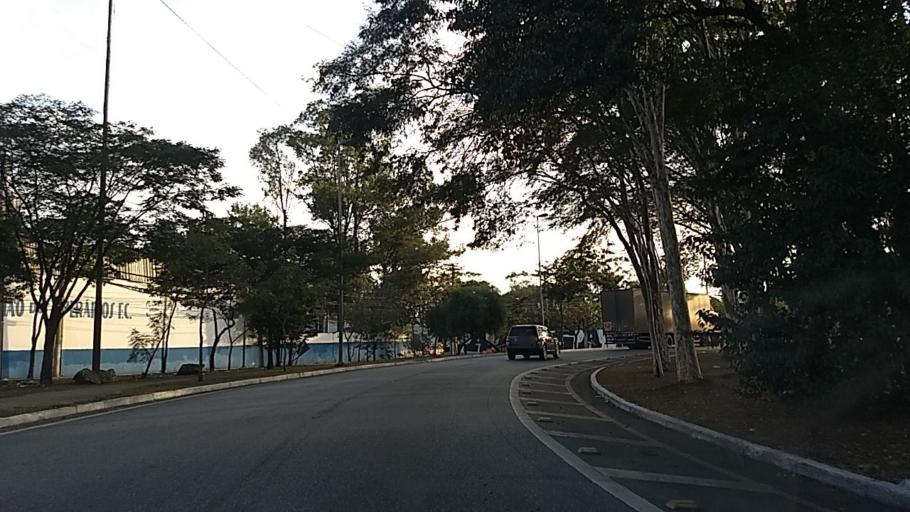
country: BR
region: Sao Paulo
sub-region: Sao Paulo
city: Sao Paulo
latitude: -23.5295
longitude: -46.5969
